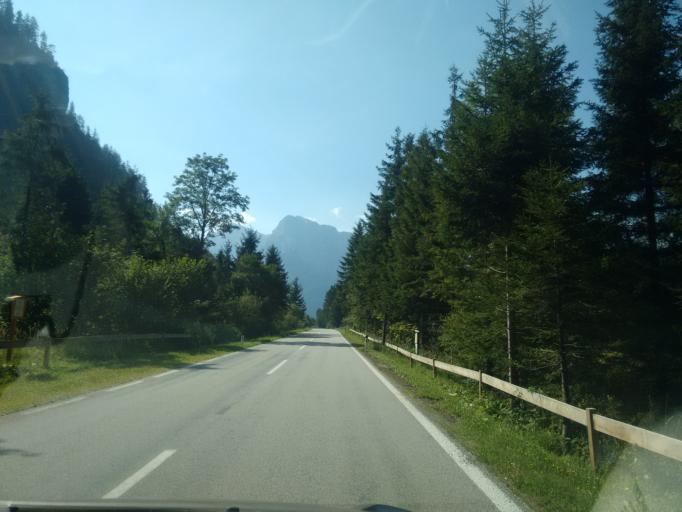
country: AT
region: Upper Austria
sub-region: Politischer Bezirk Gmunden
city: Gruenau im Almtal
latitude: 47.7721
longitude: 13.9571
